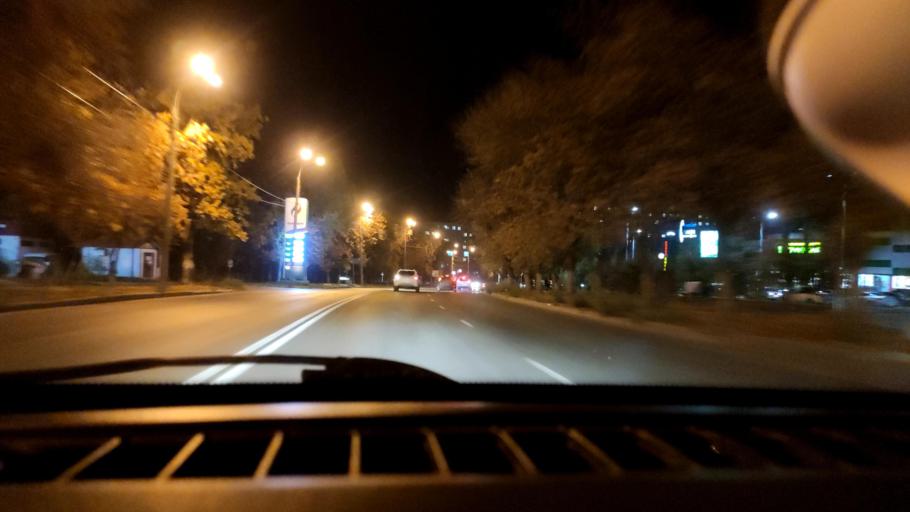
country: RU
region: Samara
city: Samara
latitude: 53.2495
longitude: 50.2408
